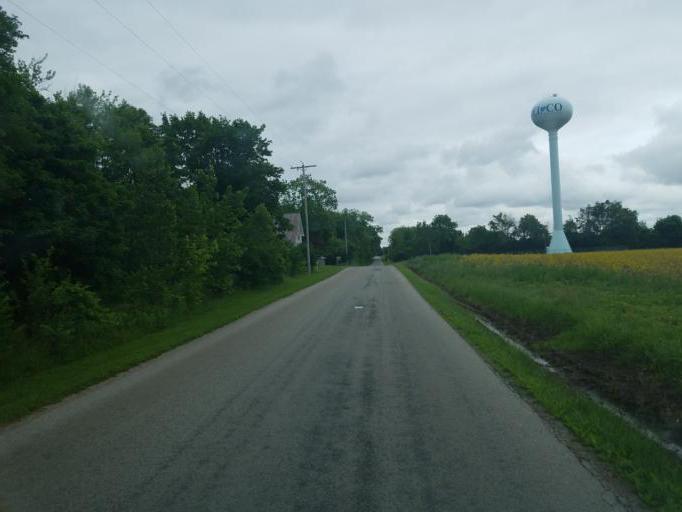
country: US
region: Ohio
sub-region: Morrow County
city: Mount Gilead
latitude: 40.5559
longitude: -82.8718
